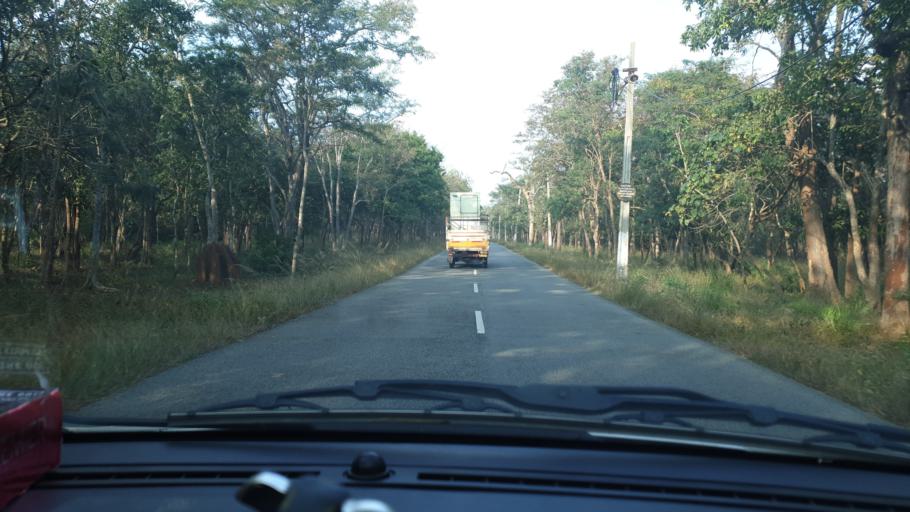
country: IN
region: Andhra Pradesh
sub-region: Kurnool
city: Srisailam
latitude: 16.2891
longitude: 78.7293
